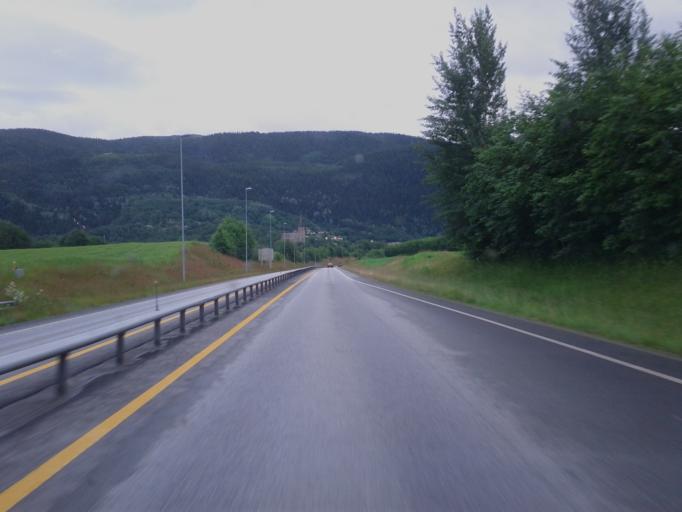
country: NO
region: Sor-Trondelag
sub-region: Melhus
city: Melhus
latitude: 63.2789
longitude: 10.2800
